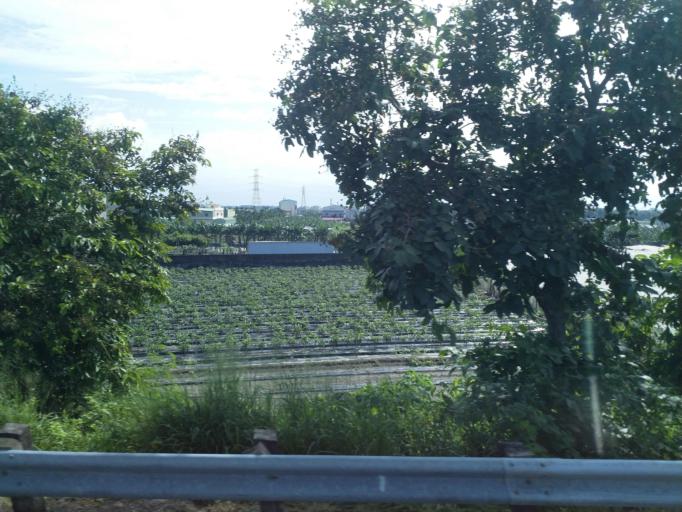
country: TW
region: Taiwan
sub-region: Pingtung
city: Pingtung
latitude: 22.8205
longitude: 120.4873
